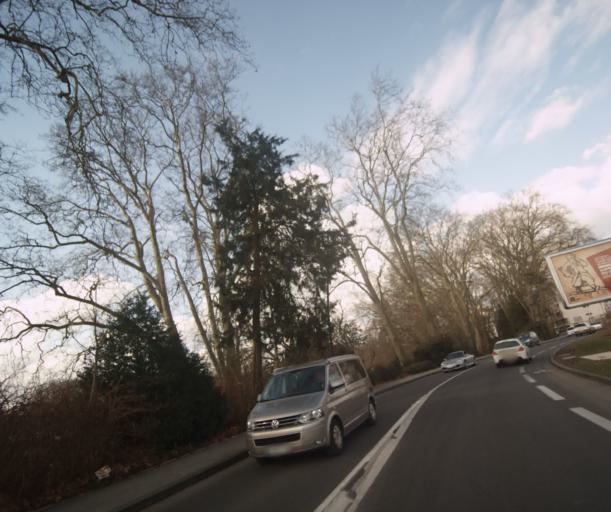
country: FR
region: Franche-Comte
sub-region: Departement du Doubs
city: Besancon
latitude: 47.2389
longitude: 6.0339
